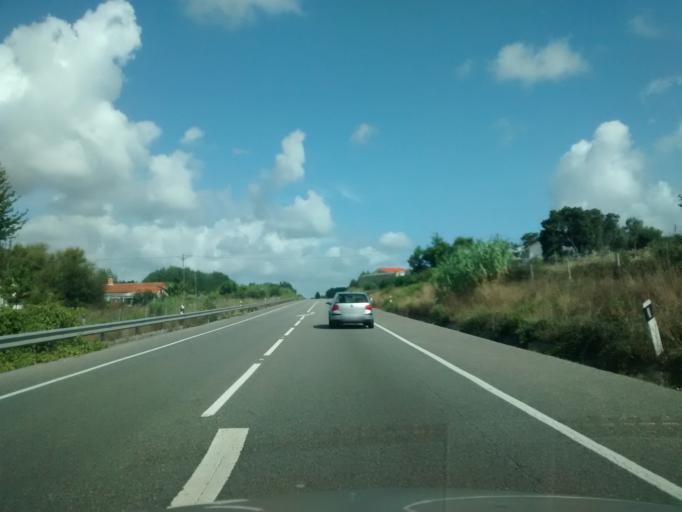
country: PT
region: Aveiro
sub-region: Anadia
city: Sangalhos
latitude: 40.4701
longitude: -8.4686
